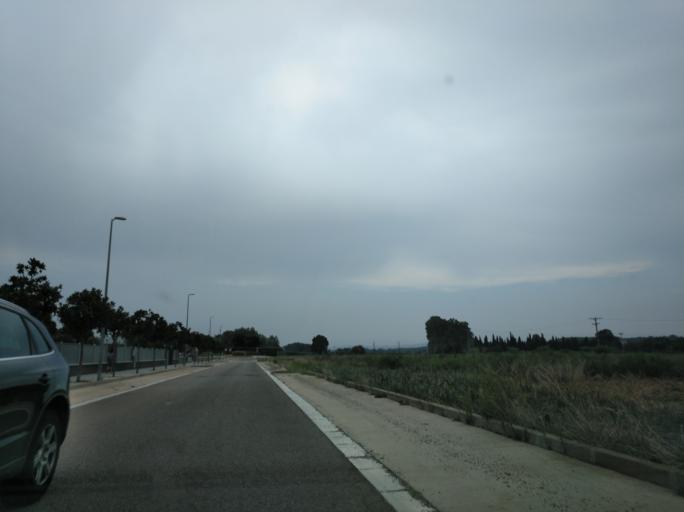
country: ES
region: Catalonia
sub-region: Provincia de Girona
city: Santa Coloma de Farners
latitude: 41.8544
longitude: 2.6757
